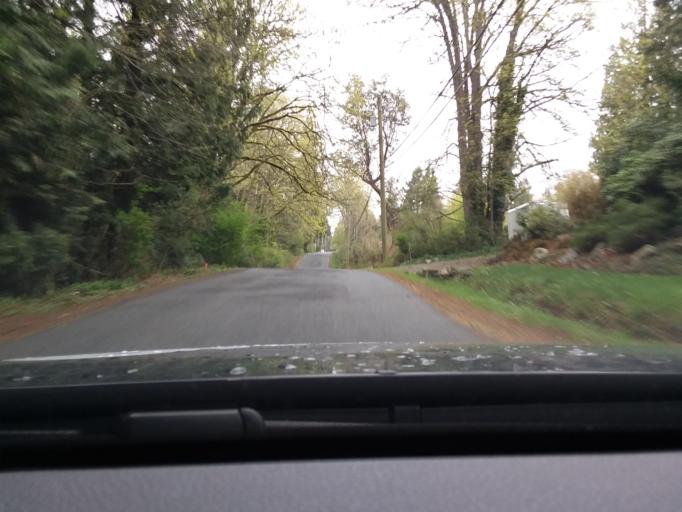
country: CA
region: British Columbia
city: Victoria
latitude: 48.5196
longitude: -123.3827
